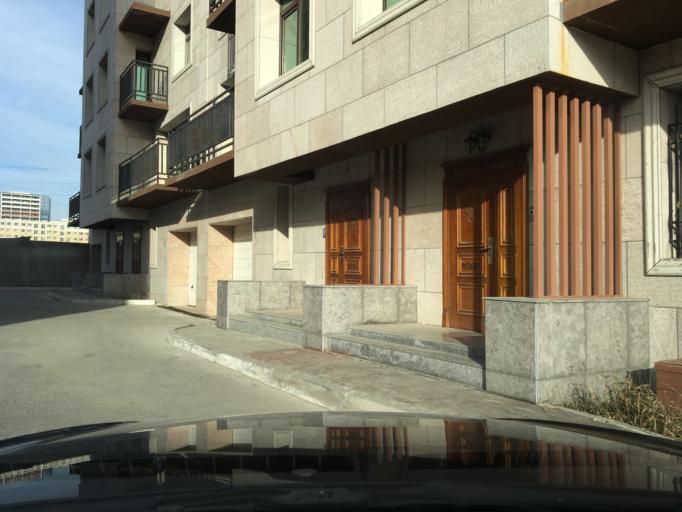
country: MN
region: Ulaanbaatar
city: Ulaanbaatar
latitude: 47.8944
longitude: 106.9187
